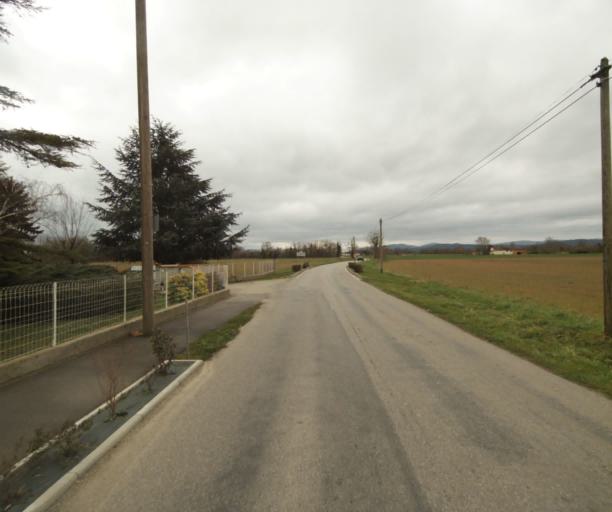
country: FR
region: Midi-Pyrenees
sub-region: Departement de l'Ariege
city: Pamiers
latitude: 43.1480
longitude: 1.6348
